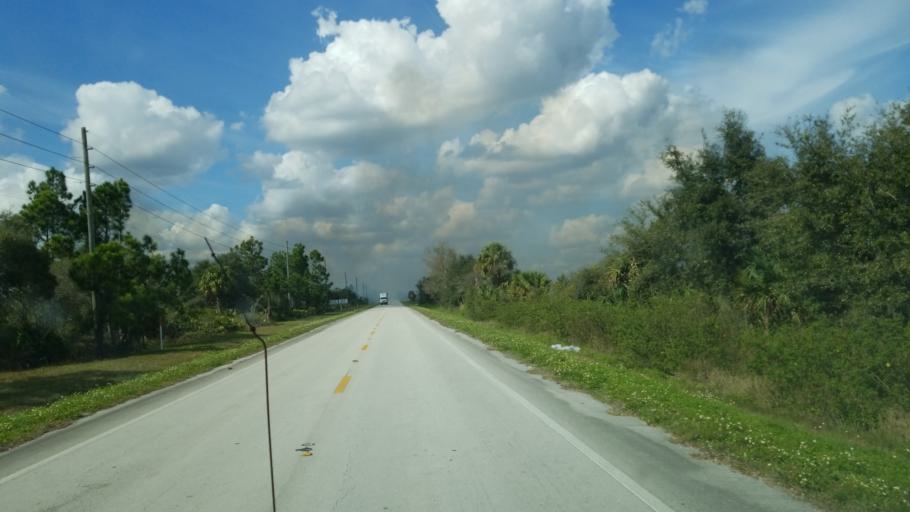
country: US
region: Florida
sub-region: Osceola County
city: Saint Cloud
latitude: 28.0435
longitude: -81.0488
